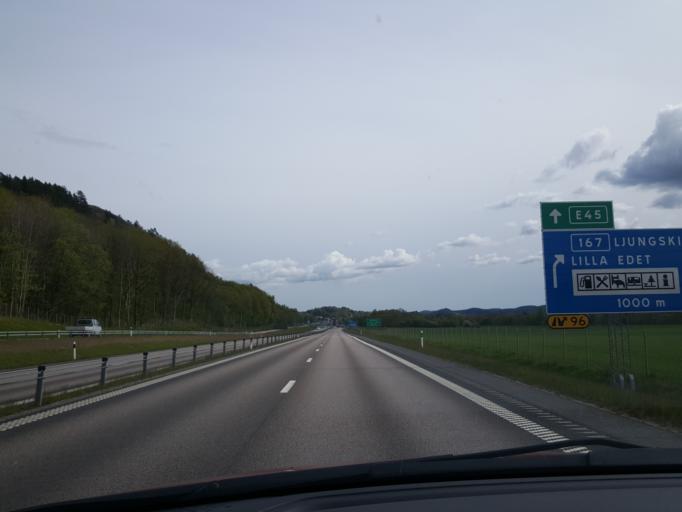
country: SE
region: Vaestra Goetaland
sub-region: Lilla Edets Kommun
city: Lilla Edet
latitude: 58.1595
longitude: 12.1360
